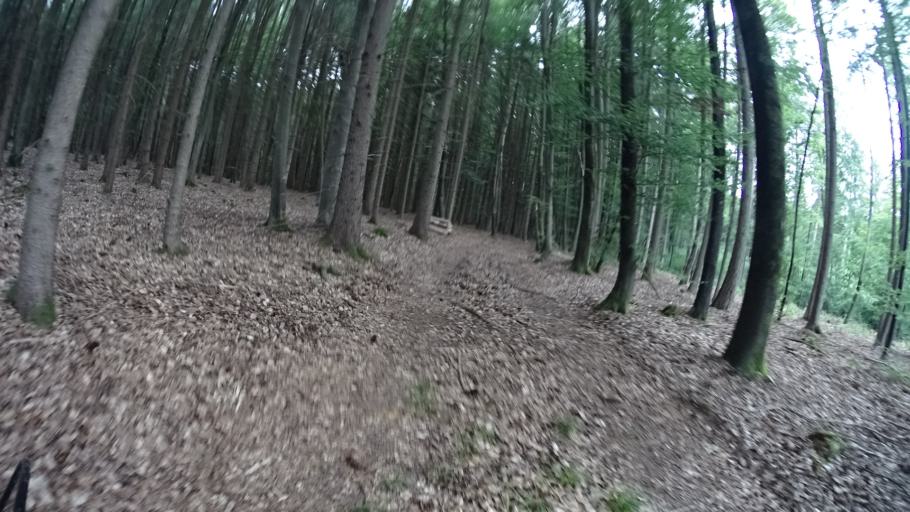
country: DE
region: Bavaria
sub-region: Upper Bavaria
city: Walting
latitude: 48.9135
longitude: 11.3330
